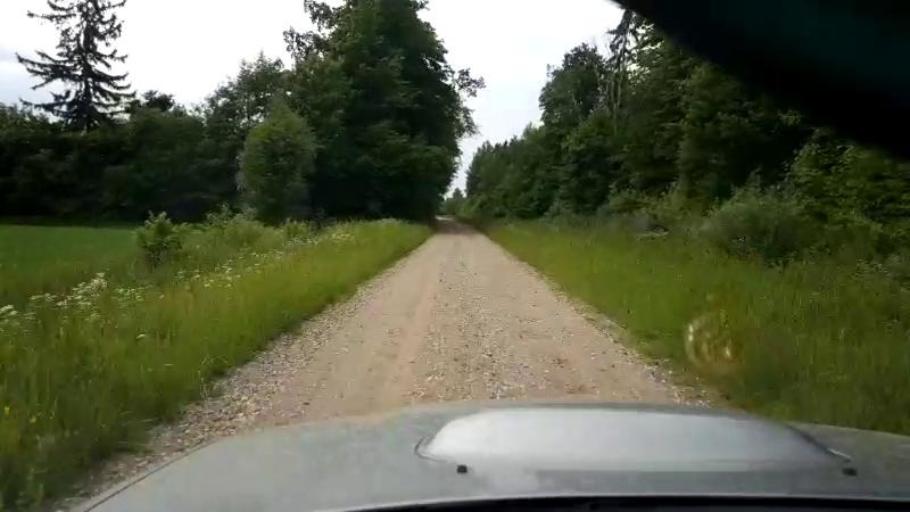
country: EE
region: Paernumaa
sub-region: Tootsi vald
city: Tootsi
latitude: 58.5459
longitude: 24.7403
